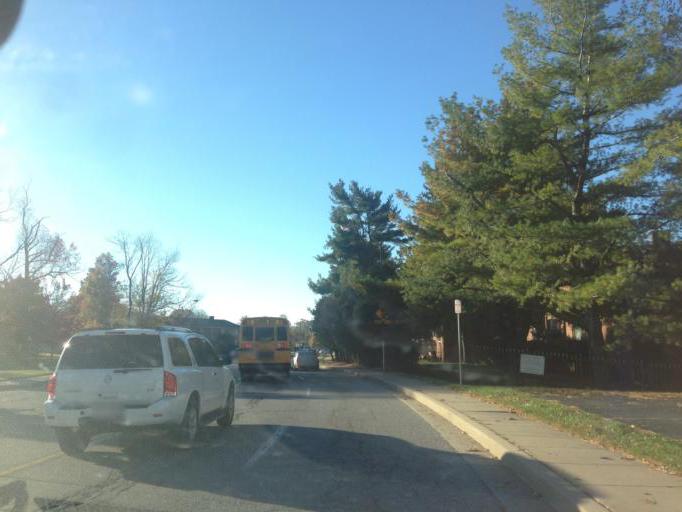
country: US
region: Maryland
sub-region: Baltimore County
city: Pikesville
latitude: 39.3660
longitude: -76.7204
